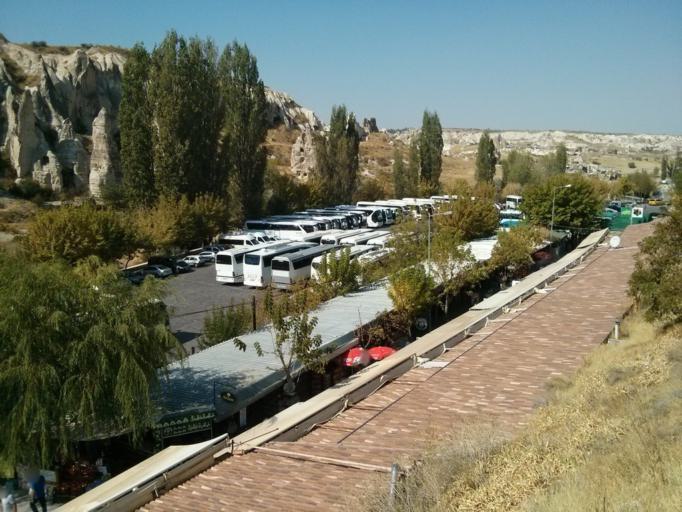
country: TR
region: Nevsehir
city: Goereme
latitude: 38.6412
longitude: 34.8443
